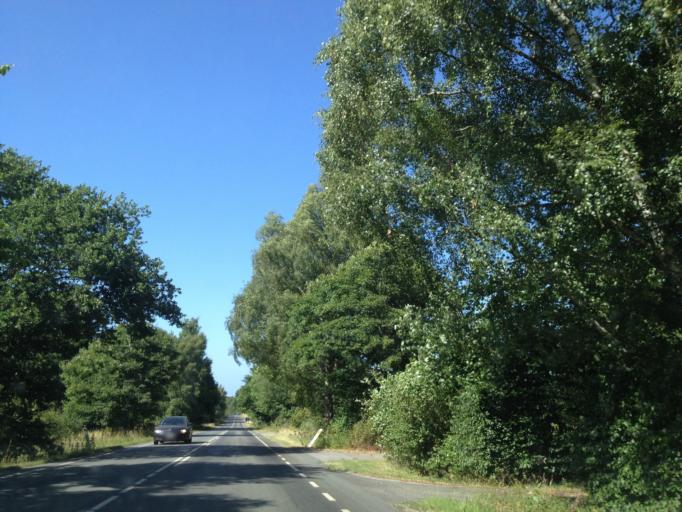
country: DK
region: Capital Region
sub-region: Hillerod Kommune
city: Nodebo
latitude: 56.0403
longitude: 12.3453
